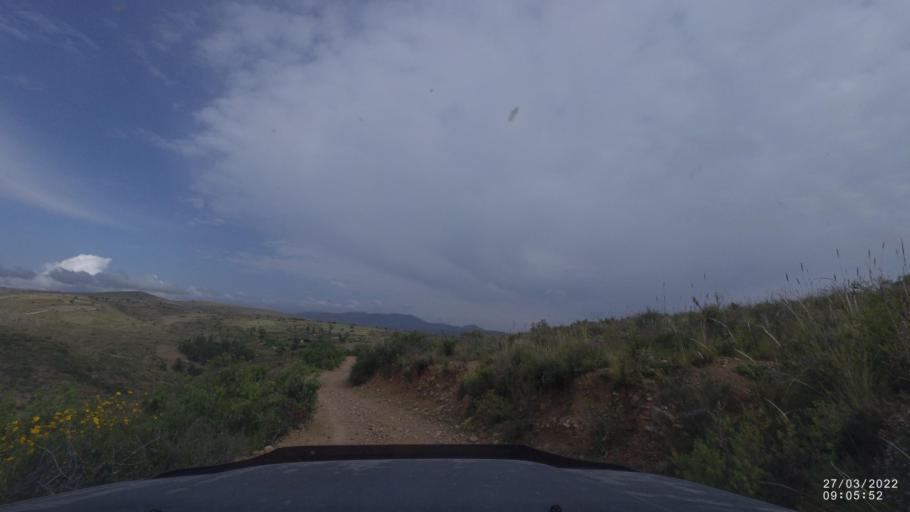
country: BO
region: Cochabamba
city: Cliza
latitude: -17.7316
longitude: -65.8694
